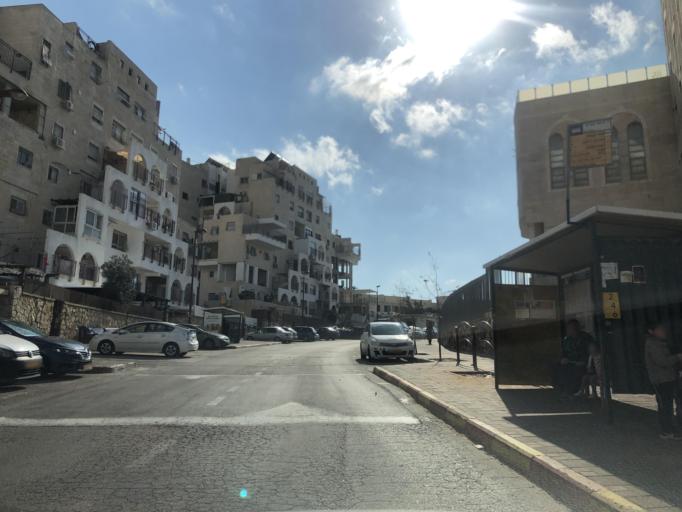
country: PS
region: West Bank
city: Dayr Qiddis
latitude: 31.9407
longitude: 35.0452
